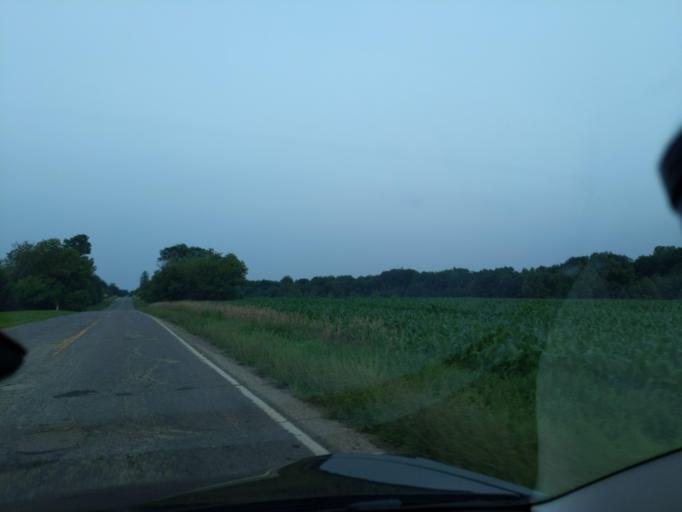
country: US
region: Michigan
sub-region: Jackson County
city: Jackson
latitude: 42.3275
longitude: -84.4334
